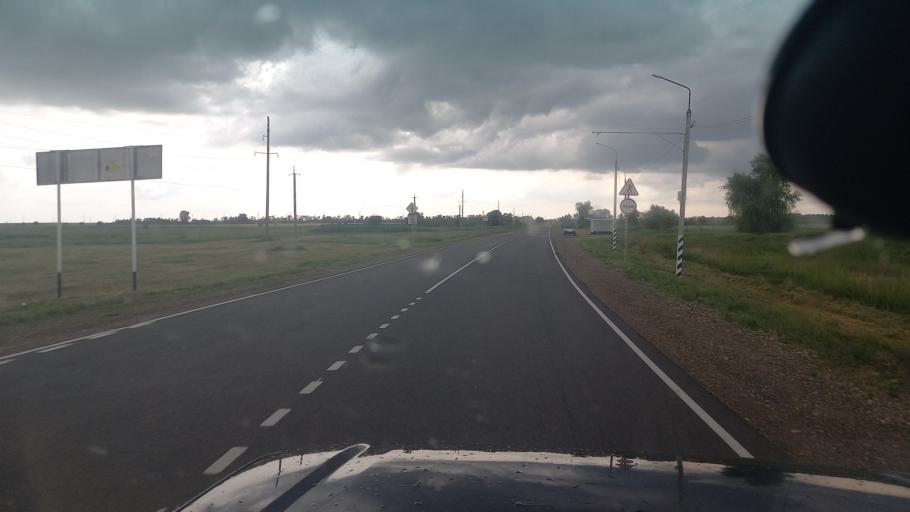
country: RU
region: Adygeya
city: Shovgenovskiy
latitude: 45.0116
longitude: 40.1988
